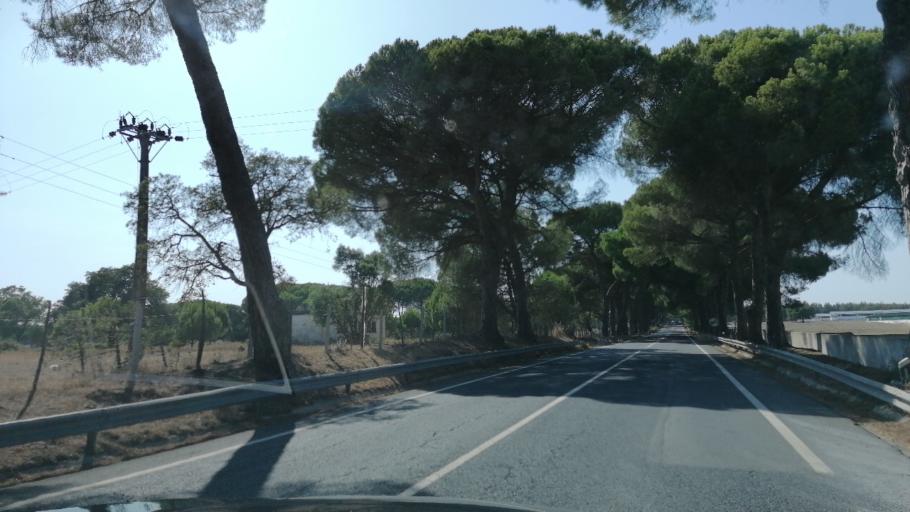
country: PT
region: Evora
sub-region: Vendas Novas
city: Vendas Novas
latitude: 38.7183
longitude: -8.6226
